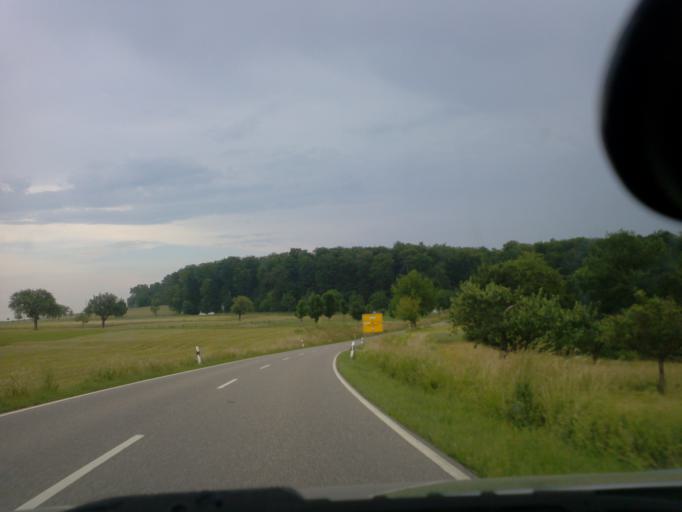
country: DE
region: Baden-Wuerttemberg
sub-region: Karlsruhe Region
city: Eisingen
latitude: 48.9734
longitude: 8.7032
